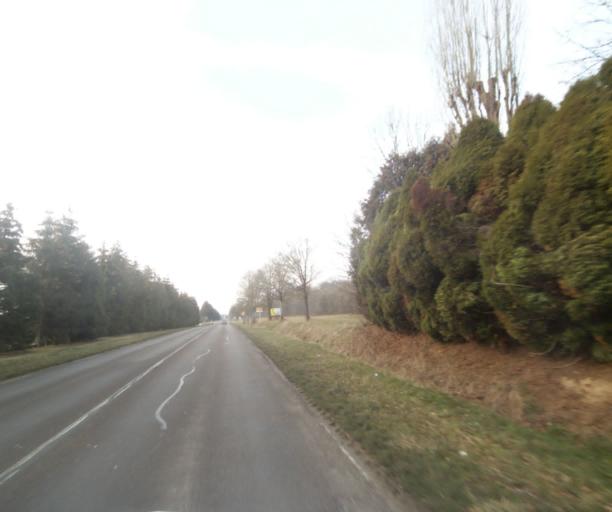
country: FR
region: Champagne-Ardenne
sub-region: Departement de la Haute-Marne
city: Bettancourt-la-Ferree
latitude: 48.6618
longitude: 4.9753
